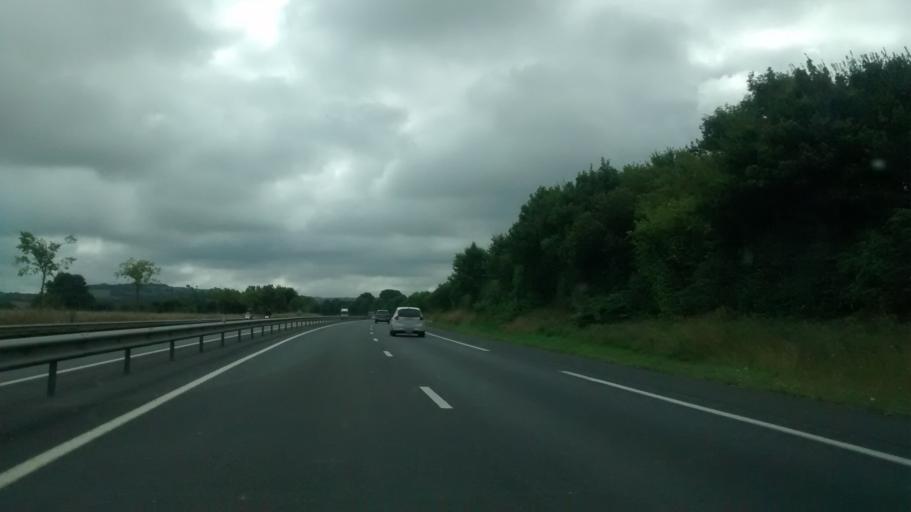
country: FR
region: Lower Normandy
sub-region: Departement du Calvados
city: Saint-Martin-des-Besaces
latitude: 49.0148
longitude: -0.8661
